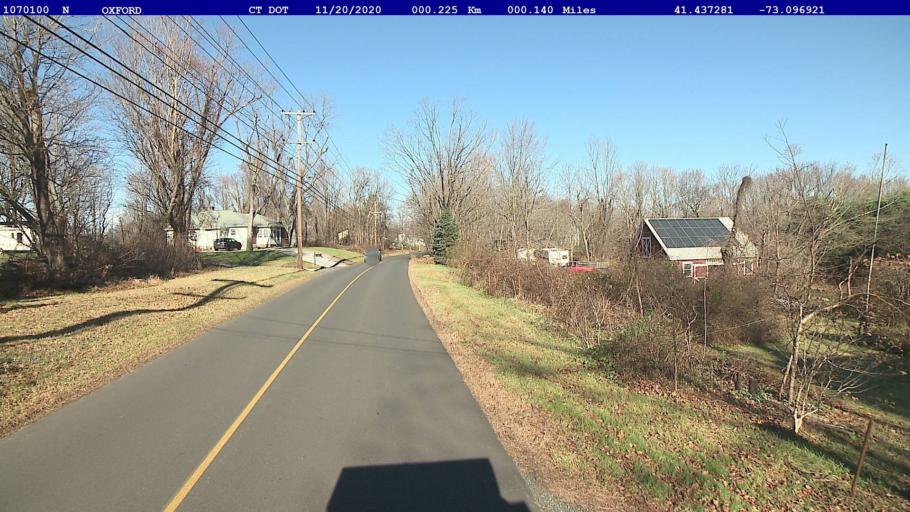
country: US
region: Connecticut
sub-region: New Haven County
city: Oxford
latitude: 41.4373
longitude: -73.0969
